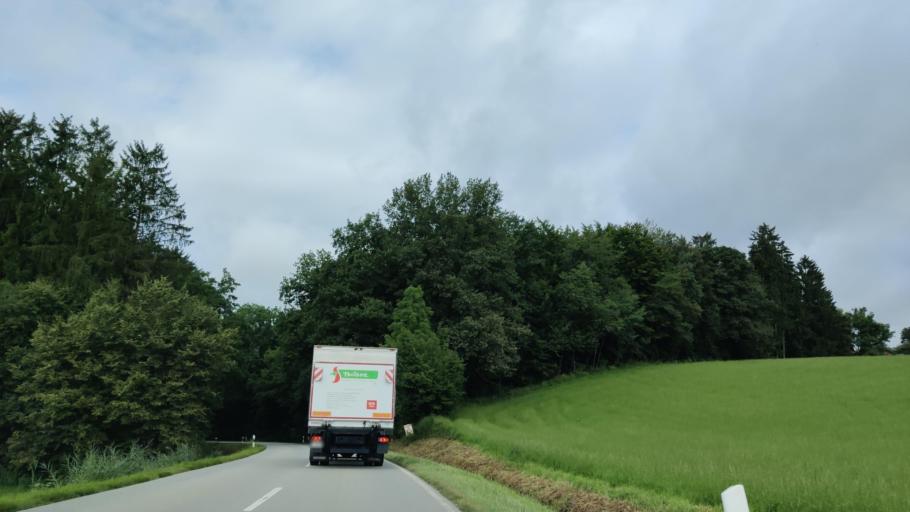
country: DE
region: Bavaria
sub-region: Lower Bavaria
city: Hofkirchen
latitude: 48.6806
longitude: 13.1449
